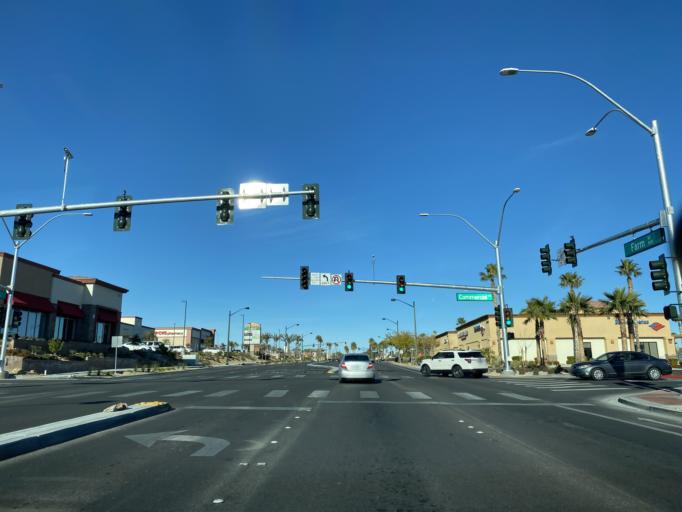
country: US
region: Nevada
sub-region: Clark County
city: Summerlin South
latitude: 36.2997
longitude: -115.2808
